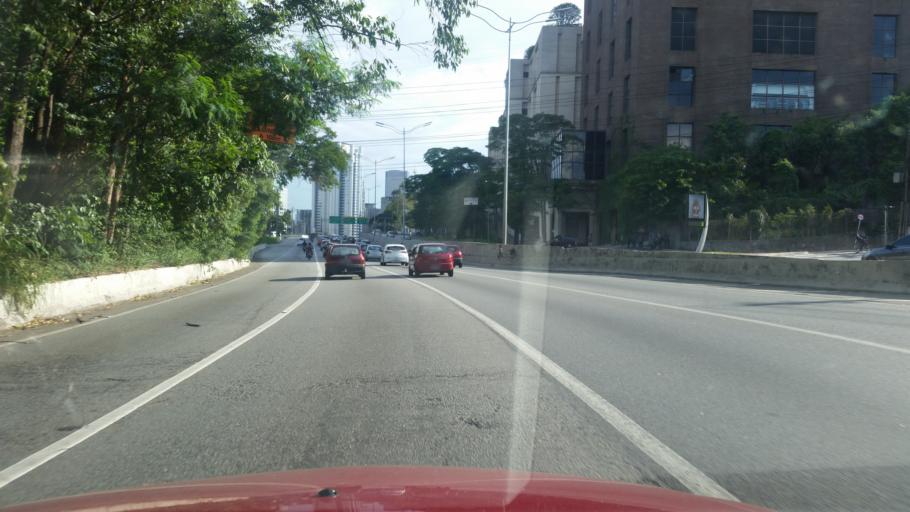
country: BR
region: Sao Paulo
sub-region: Sao Paulo
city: Sao Paulo
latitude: -23.5971
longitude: -46.6971
